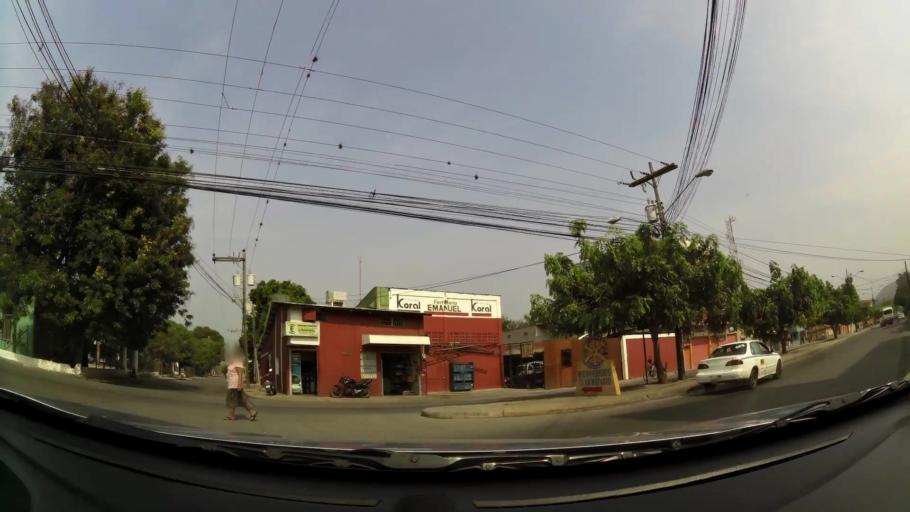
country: HN
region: Comayagua
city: Comayagua
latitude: 14.4600
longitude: -87.6448
